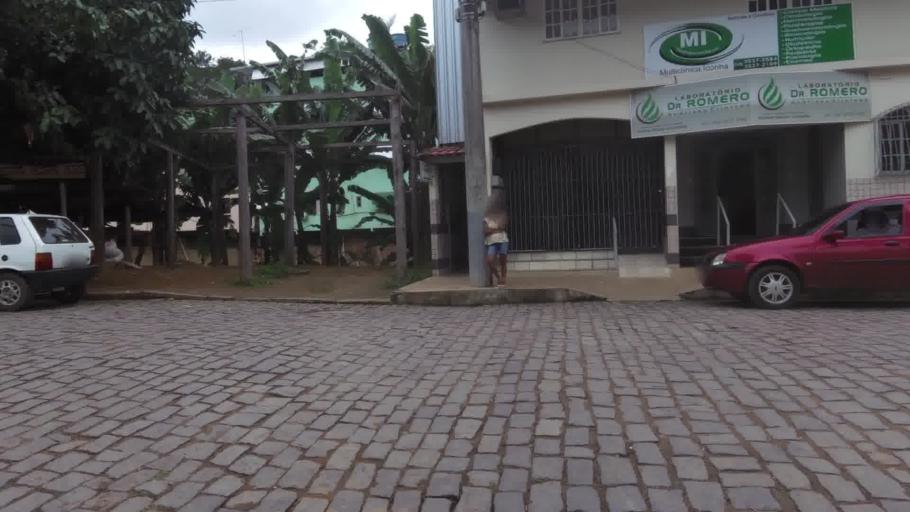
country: BR
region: Espirito Santo
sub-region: Iconha
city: Iconha
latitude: -20.7916
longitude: -40.8128
